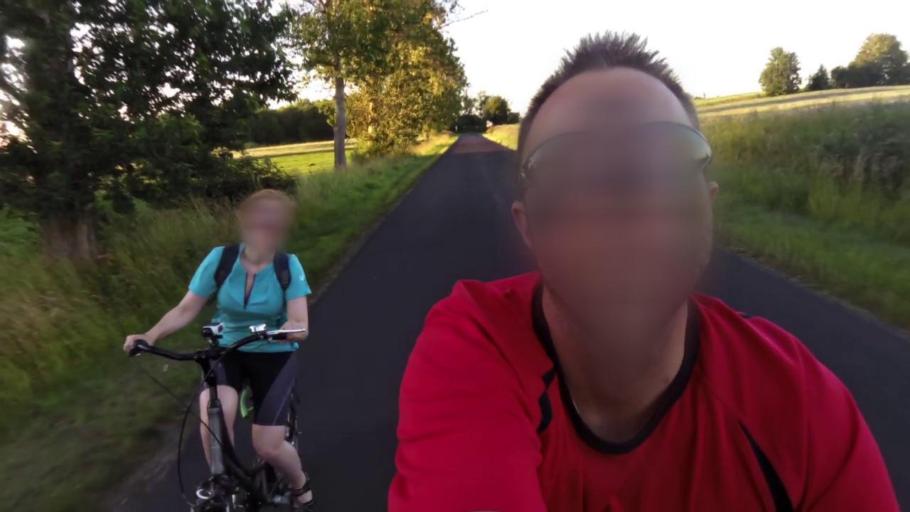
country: PL
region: West Pomeranian Voivodeship
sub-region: Powiat bialogardzki
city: Bialogard
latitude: 54.0360
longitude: 16.0449
